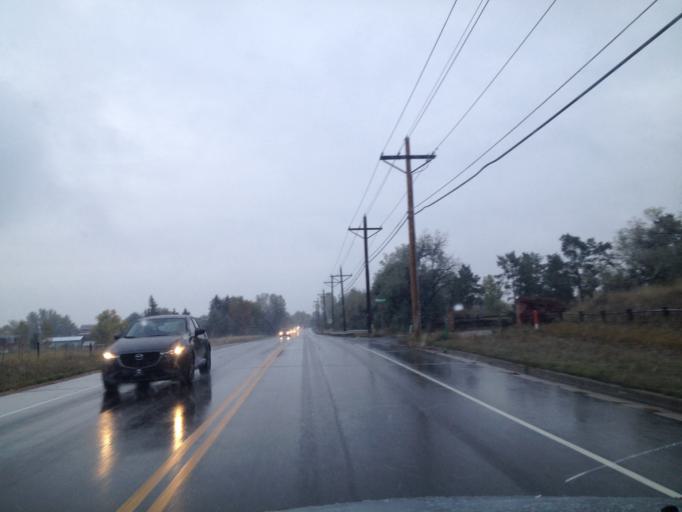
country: US
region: Colorado
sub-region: Boulder County
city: Superior
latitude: 39.9950
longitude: -105.1751
